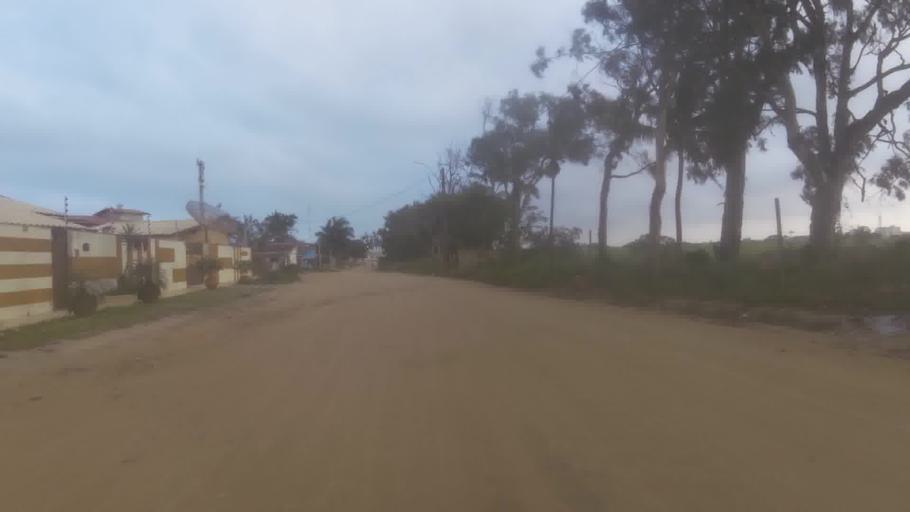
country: BR
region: Espirito Santo
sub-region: Marataizes
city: Marataizes
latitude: -21.0366
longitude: -40.8237
